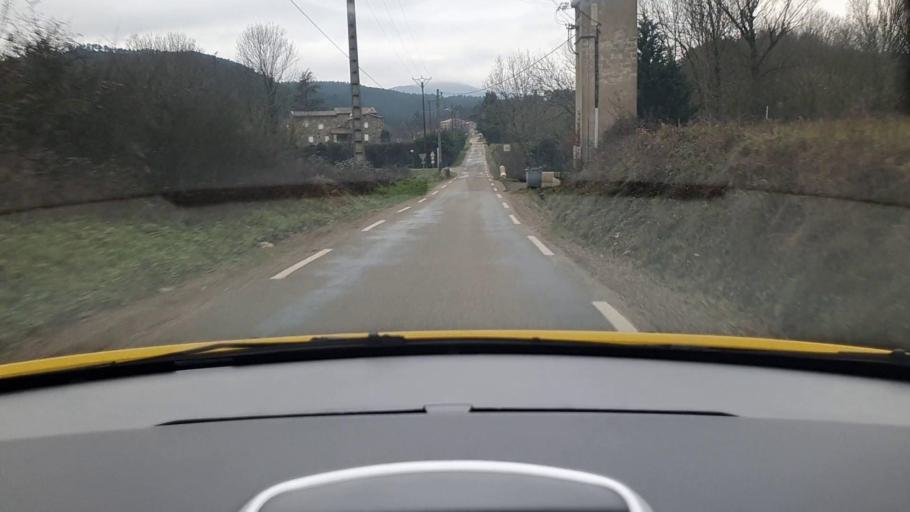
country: FR
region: Languedoc-Roussillon
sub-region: Departement du Gard
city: Besseges
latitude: 44.3196
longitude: 4.1289
